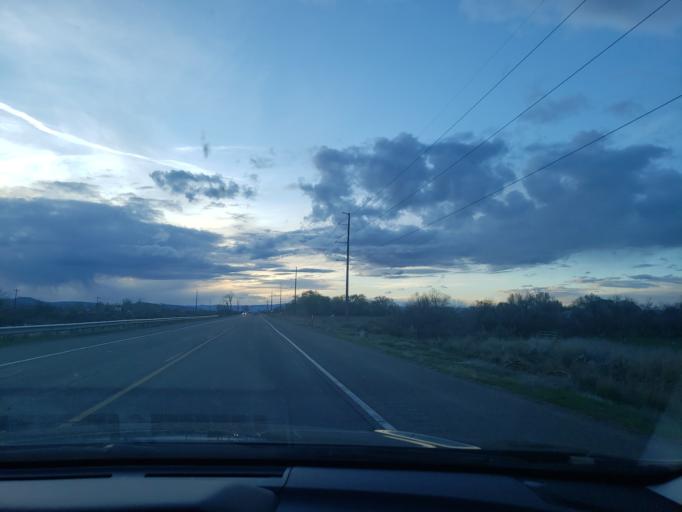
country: US
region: Colorado
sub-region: Mesa County
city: Fruita
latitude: 39.1367
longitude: -108.6967
